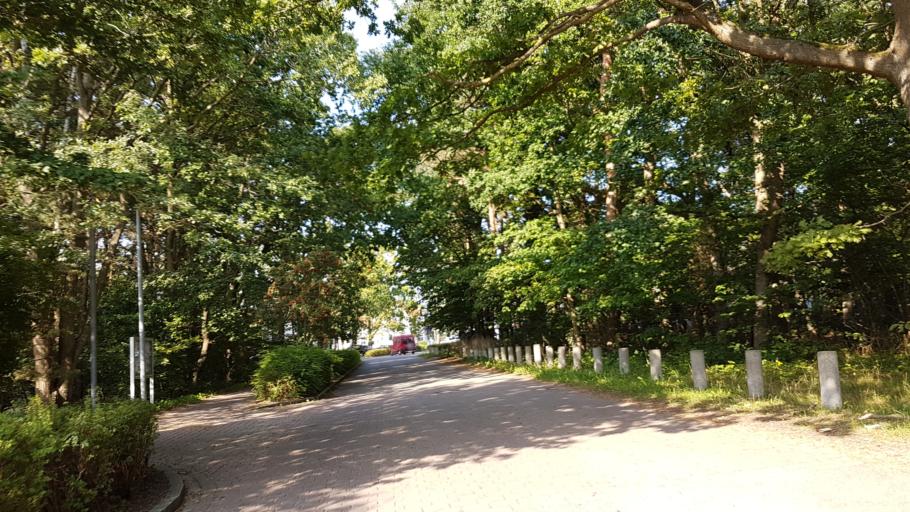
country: DE
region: Mecklenburg-Vorpommern
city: Glowe
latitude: 54.5672
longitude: 13.4589
